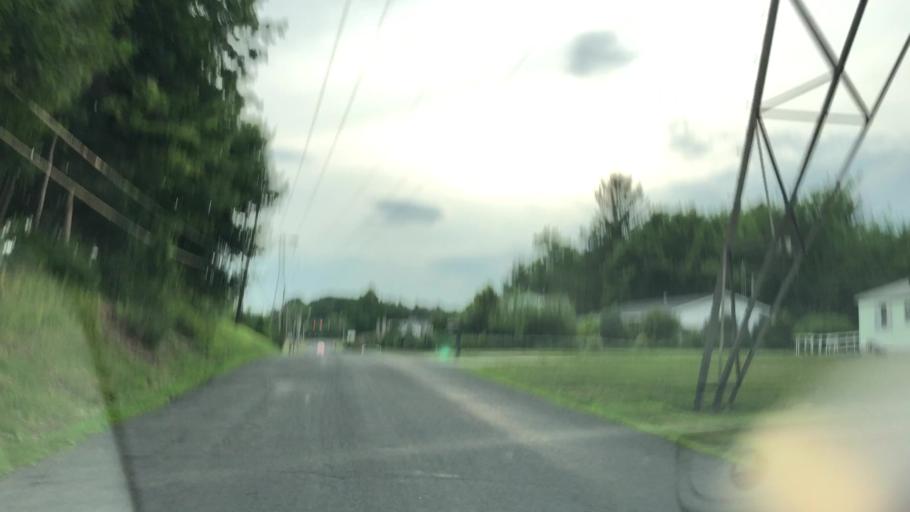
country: US
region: Ohio
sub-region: Stark County
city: North Canton
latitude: 40.8500
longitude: -81.3892
